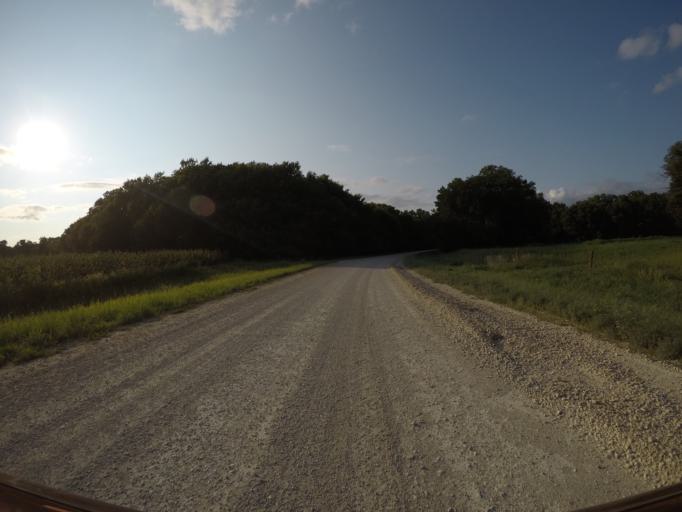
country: US
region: Kansas
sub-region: Wabaunsee County
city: Alma
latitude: 38.9565
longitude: -96.2516
